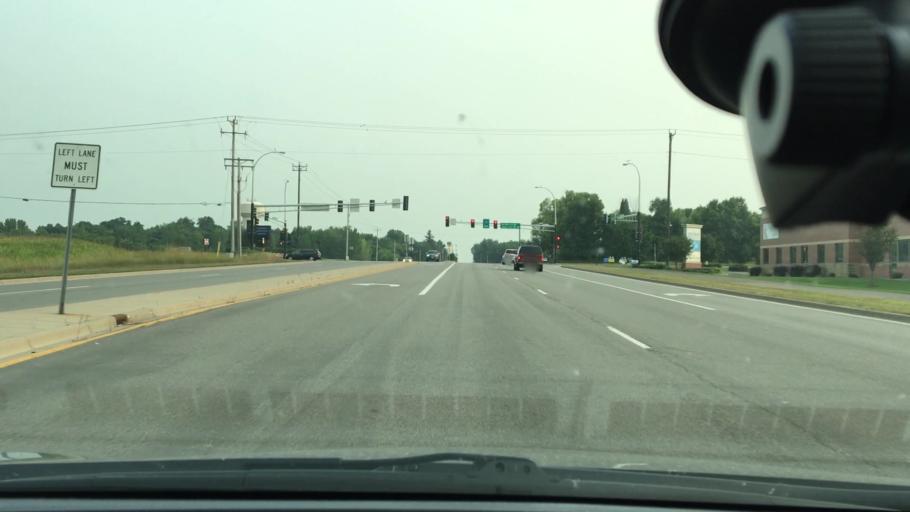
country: US
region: Minnesota
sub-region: Wright County
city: Saint Michael
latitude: 45.2256
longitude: -93.6645
